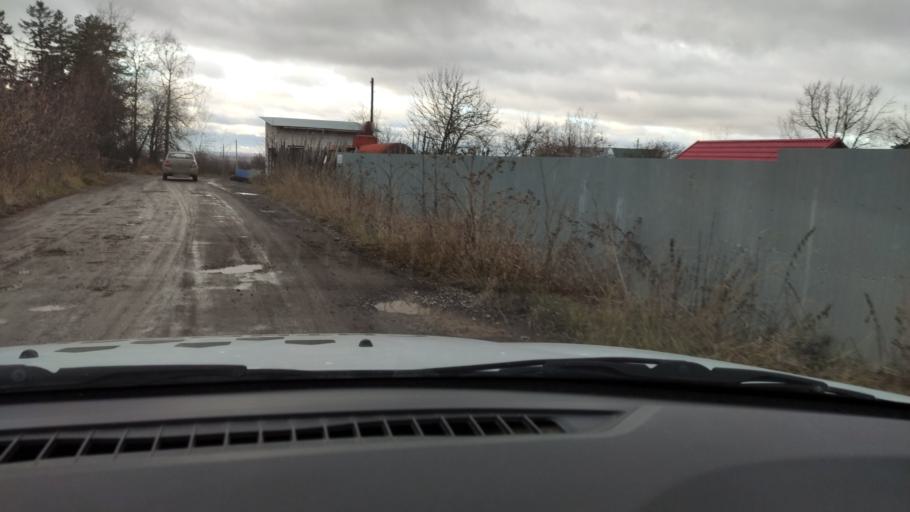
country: RU
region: Perm
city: Kondratovo
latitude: 57.9548
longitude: 56.1627
